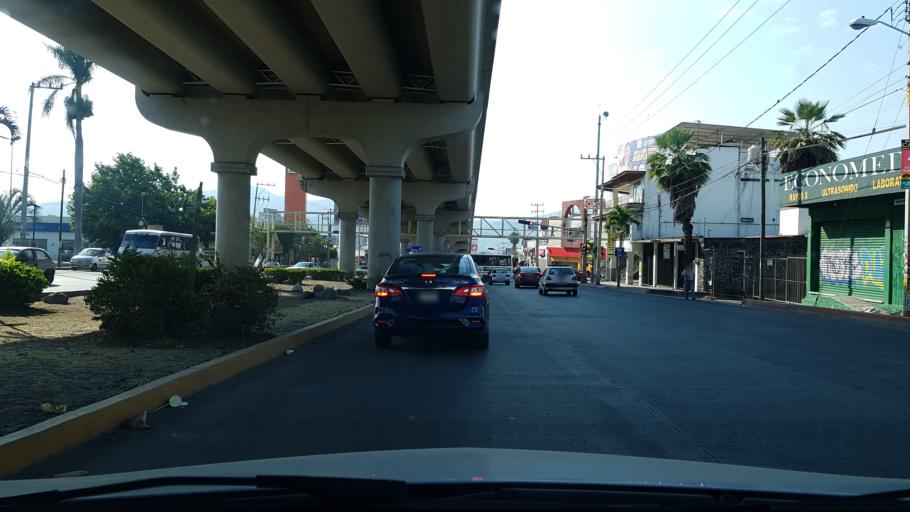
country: MX
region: Morelos
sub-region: Jiutepec
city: Jiutepec
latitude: 18.8964
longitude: -99.1681
